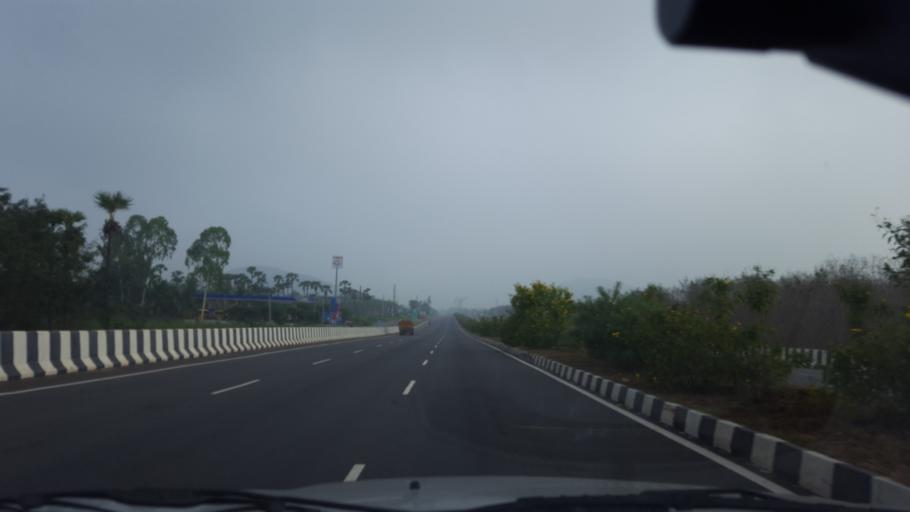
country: IN
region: Andhra Pradesh
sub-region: Prakasam
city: pedda nakkalapalem
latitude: 15.8689
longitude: 80.0633
